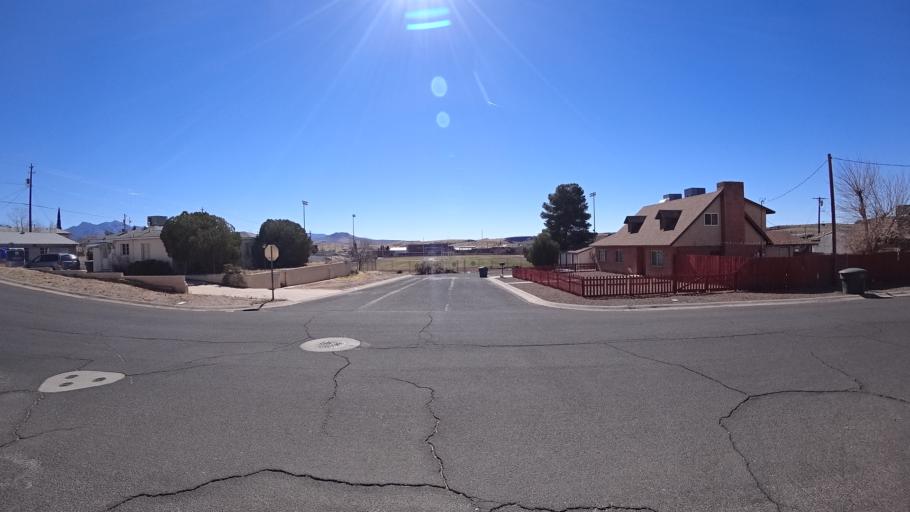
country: US
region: Arizona
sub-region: Mohave County
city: Kingman
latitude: 35.1946
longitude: -114.0588
